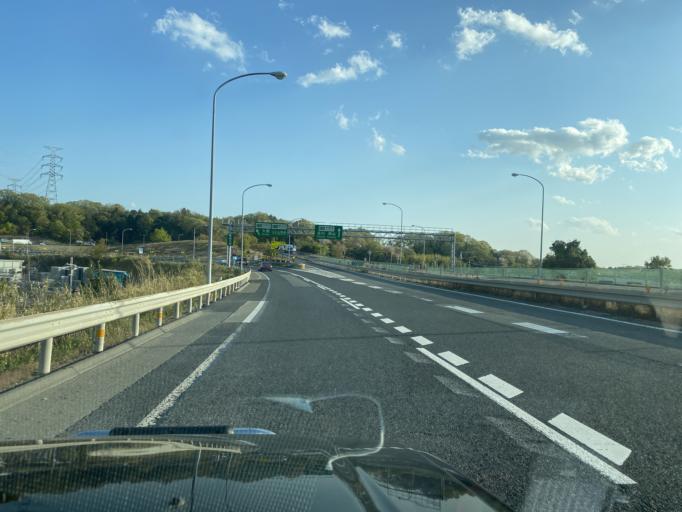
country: JP
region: Hyogo
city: Sandacho
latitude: 34.8959
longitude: 135.1521
